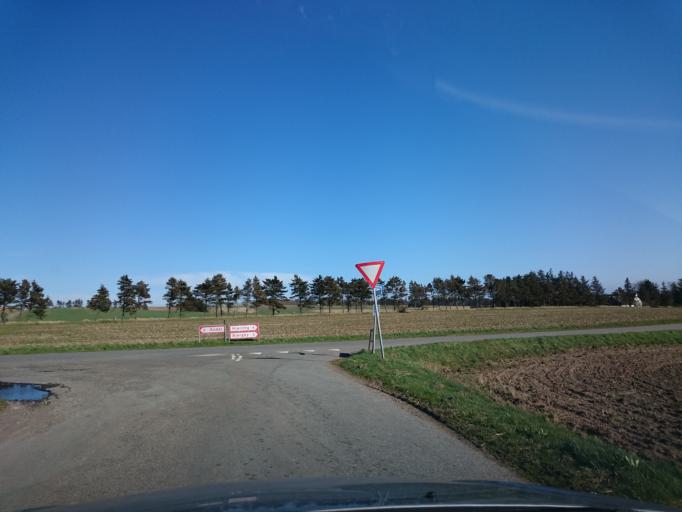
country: DK
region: North Denmark
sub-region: Hjorring Kommune
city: Hjorring
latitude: 57.5262
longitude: 10.0161
